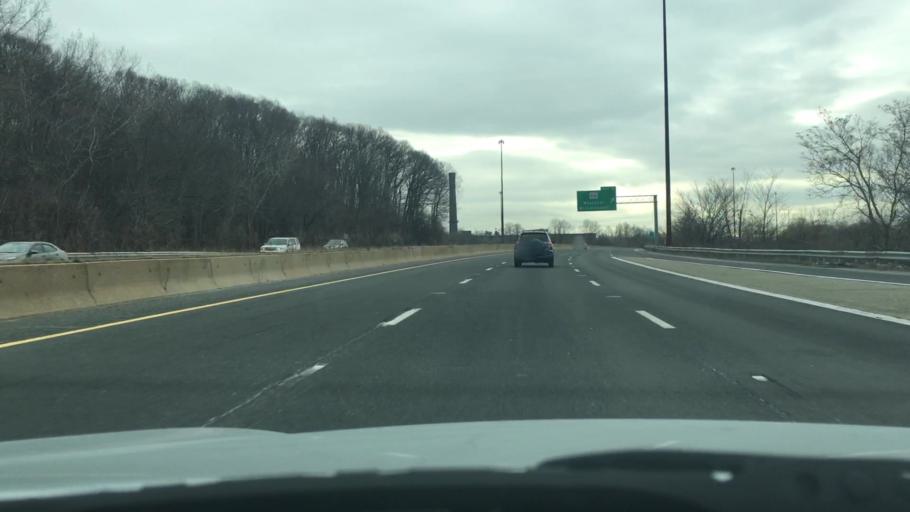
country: US
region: Massachusetts
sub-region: Hampden County
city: Chicopee
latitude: 42.1563
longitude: -72.6104
